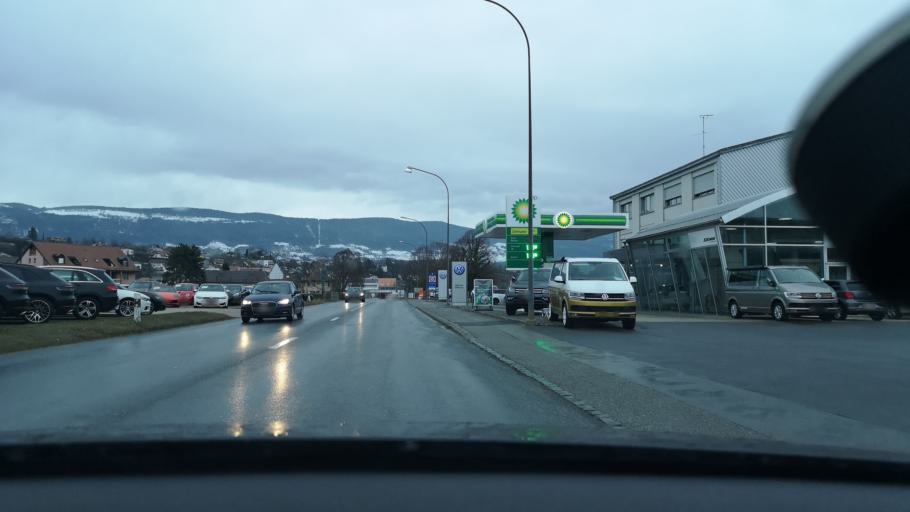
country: CH
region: Vaud
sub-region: Jura-Nord vaudois District
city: Montagny
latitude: 46.7937
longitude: 6.6279
